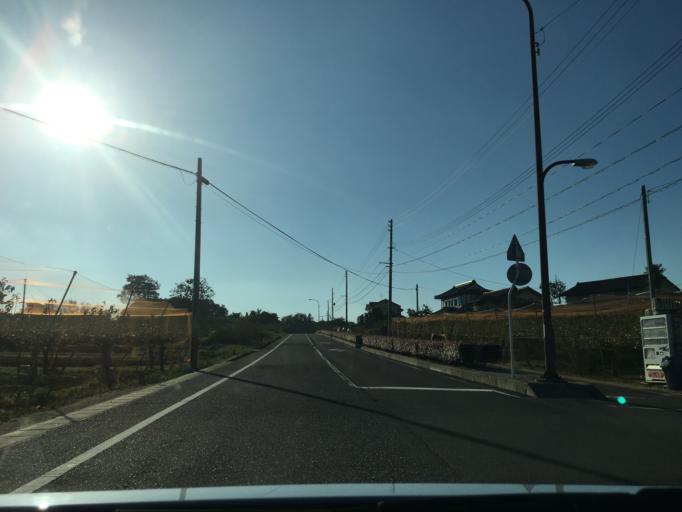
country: JP
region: Fukushima
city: Sukagawa
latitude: 37.3295
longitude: 140.3659
